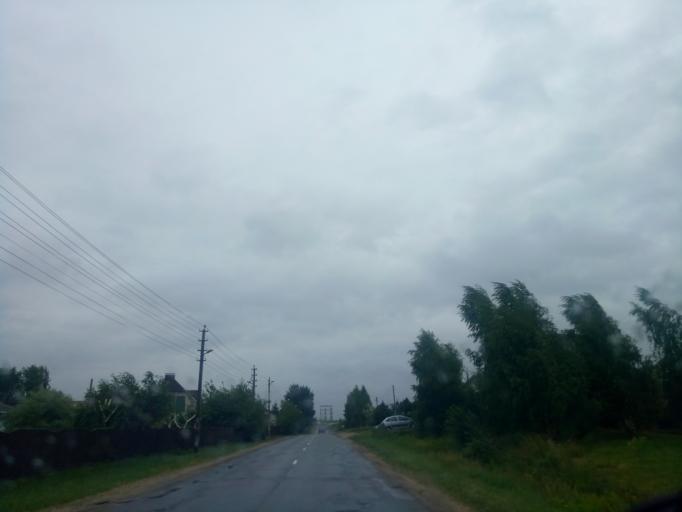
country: BY
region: Minsk
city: Zhdanovichy
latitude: 53.9331
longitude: 27.4102
